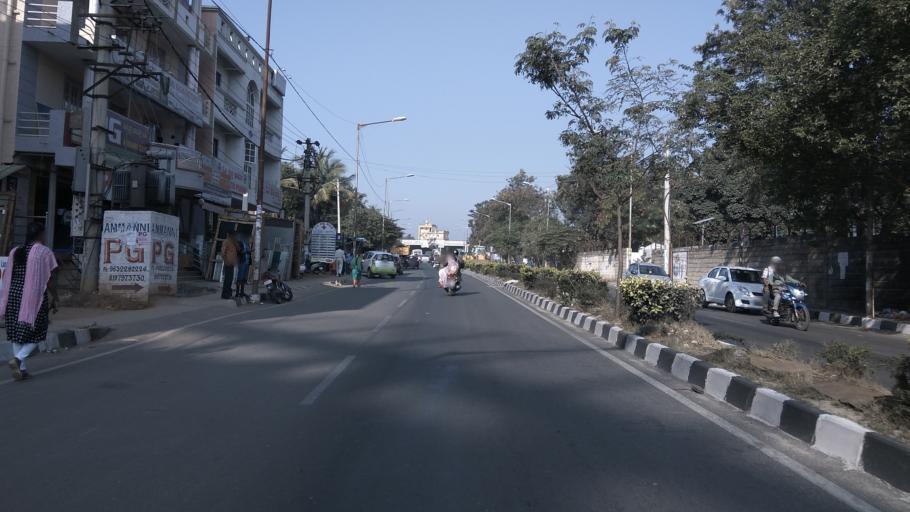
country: IN
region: Karnataka
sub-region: Bangalore Urban
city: Yelahanka
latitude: 13.1217
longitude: 77.6130
